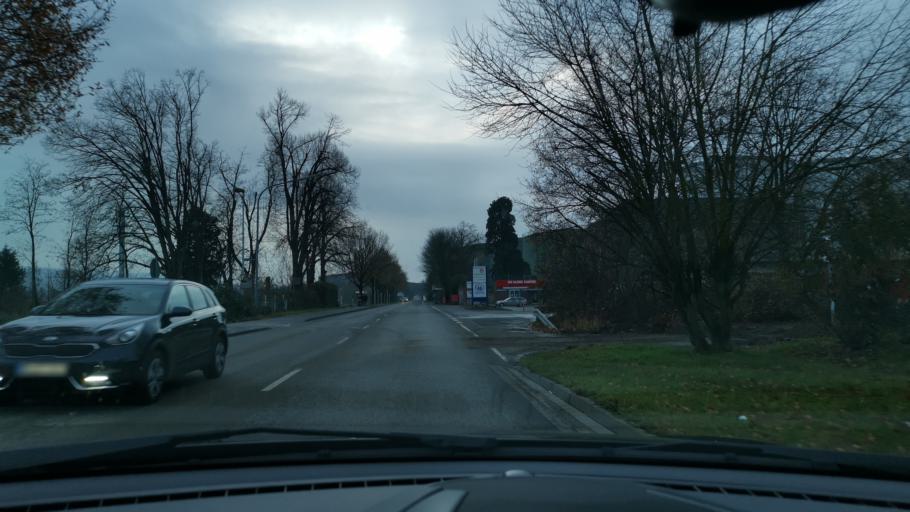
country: DE
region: North Rhine-Westphalia
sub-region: Regierungsbezirk Dusseldorf
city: Grevenbroich
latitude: 51.0945
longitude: 6.6072
